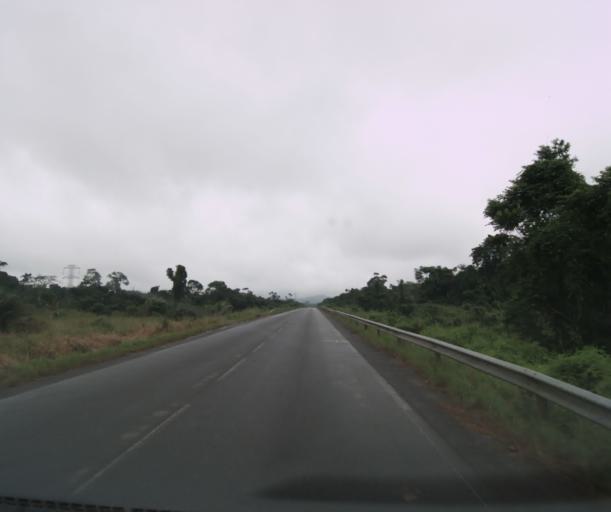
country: CM
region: Littoral
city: Edea
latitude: 3.6601
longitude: 10.1128
